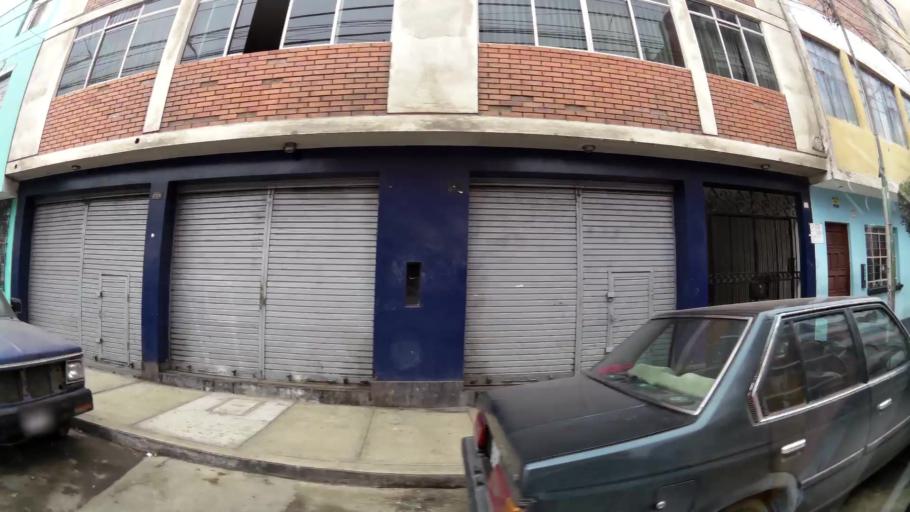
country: PE
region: Lima
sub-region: Lima
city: Surco
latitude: -12.1180
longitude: -77.0192
